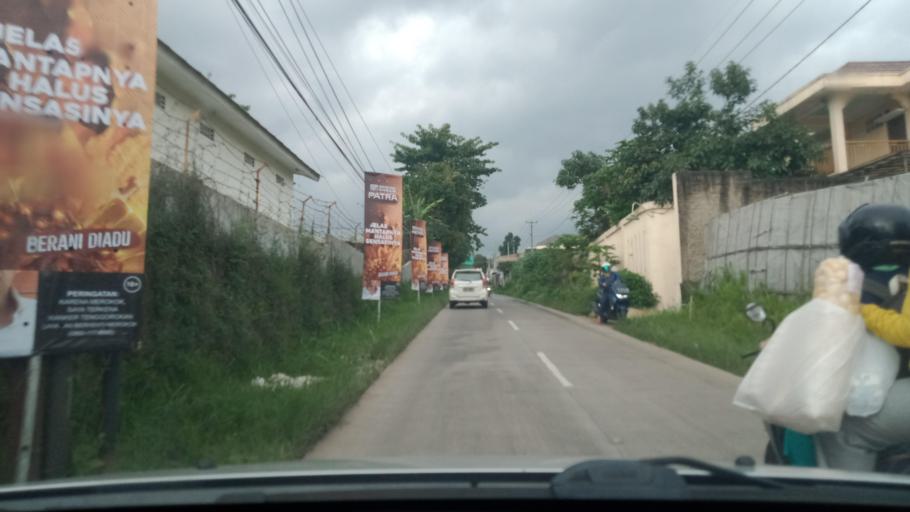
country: ID
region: West Java
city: Lembang
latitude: -6.8048
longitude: 107.5786
